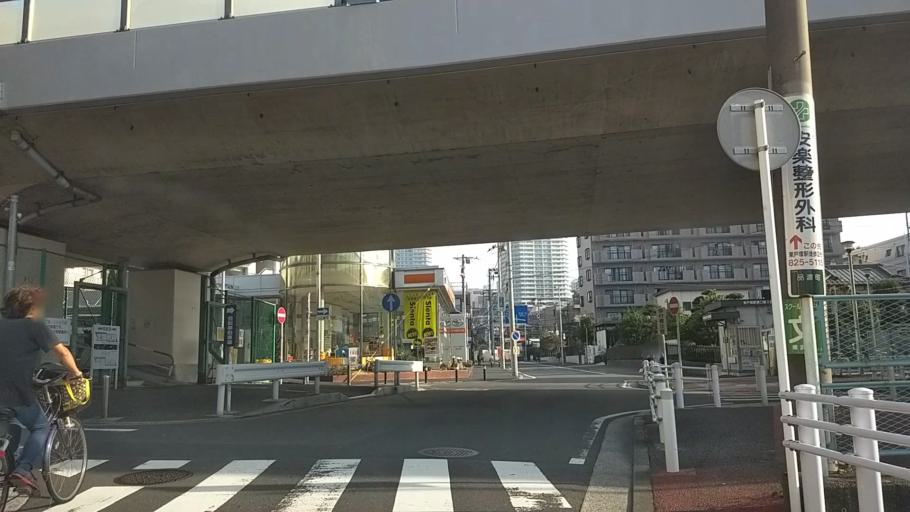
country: JP
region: Kanagawa
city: Yokohama
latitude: 35.4258
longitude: 139.5592
